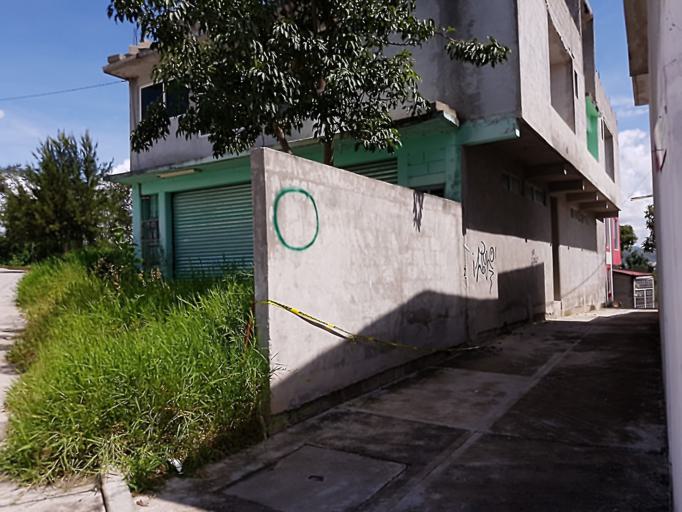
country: MX
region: Oaxaca
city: Ciudad de Huajuapam de Leon
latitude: 17.8047
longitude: -97.7961
